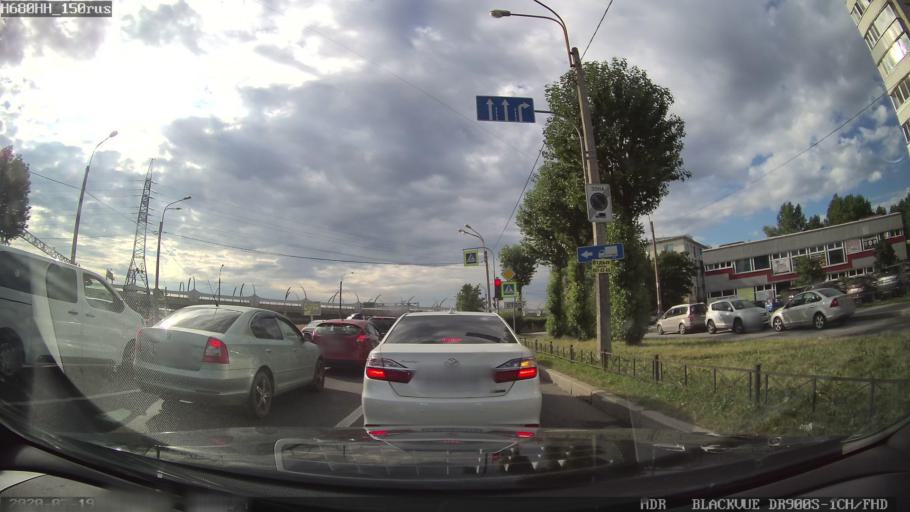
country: RU
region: St.-Petersburg
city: Avtovo
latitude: 59.8574
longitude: 30.2949
